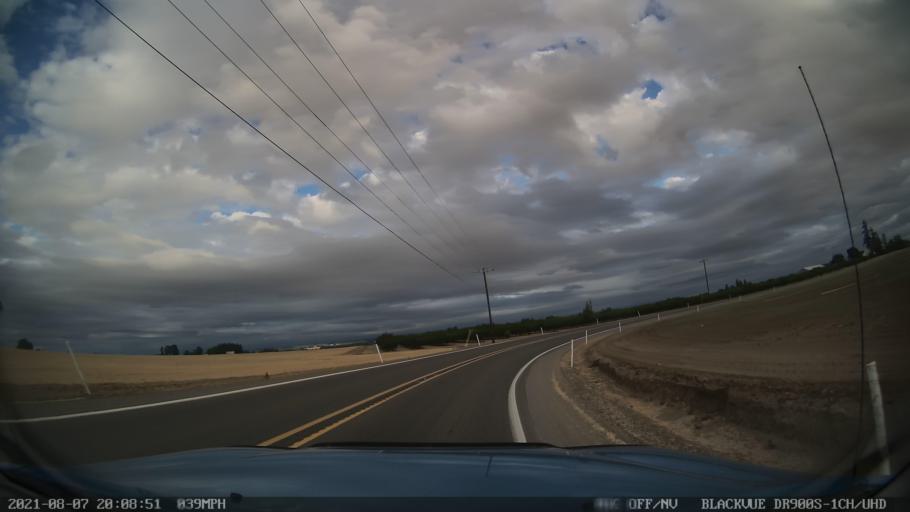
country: US
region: Oregon
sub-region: Marion County
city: Silverton
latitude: 44.9774
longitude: -122.8785
